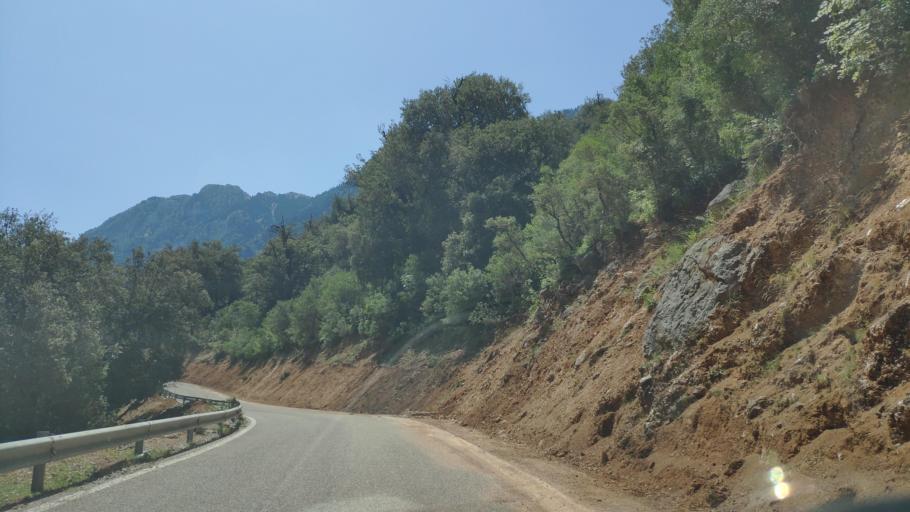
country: GR
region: West Greece
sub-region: Nomos Aitolias kai Akarnanias
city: Krikellos
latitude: 39.0162
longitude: 21.3540
